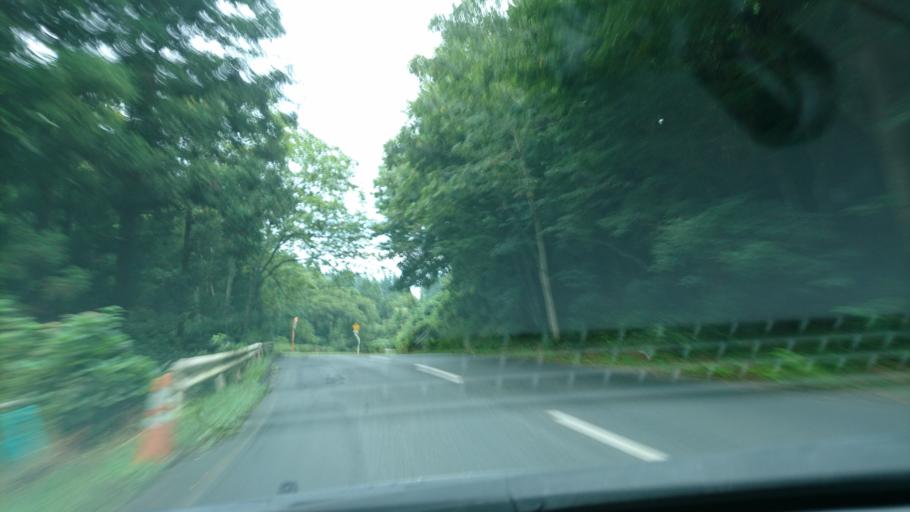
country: JP
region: Iwate
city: Mizusawa
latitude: 39.0391
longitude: 141.1908
